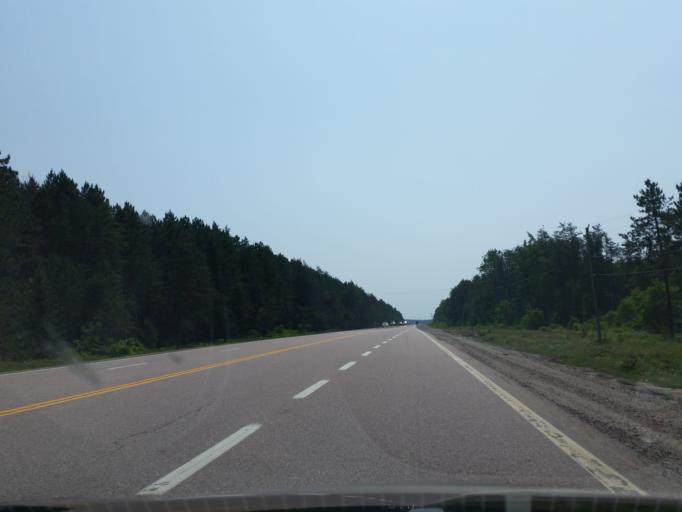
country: CA
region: Ontario
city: Deep River
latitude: 46.1768
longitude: -77.8364
